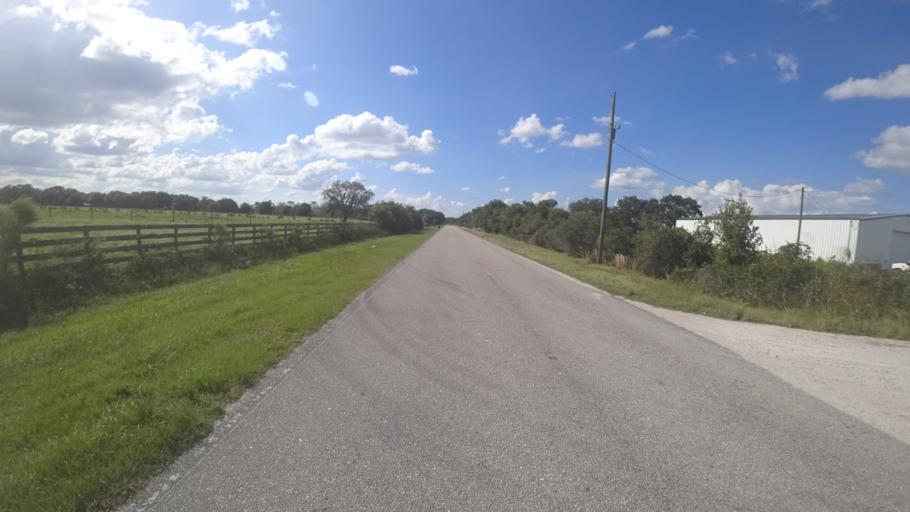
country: US
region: Florida
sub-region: DeSoto County
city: Nocatee
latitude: 27.2717
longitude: -82.1021
